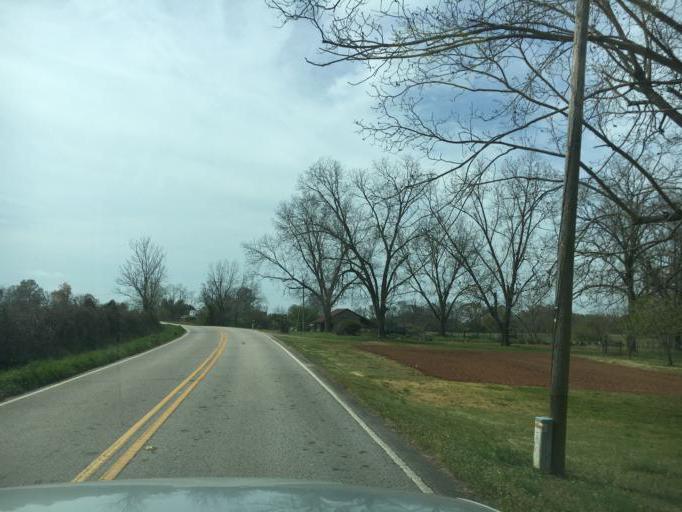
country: US
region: Georgia
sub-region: Hart County
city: Royston
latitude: 34.3146
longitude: -83.0477
